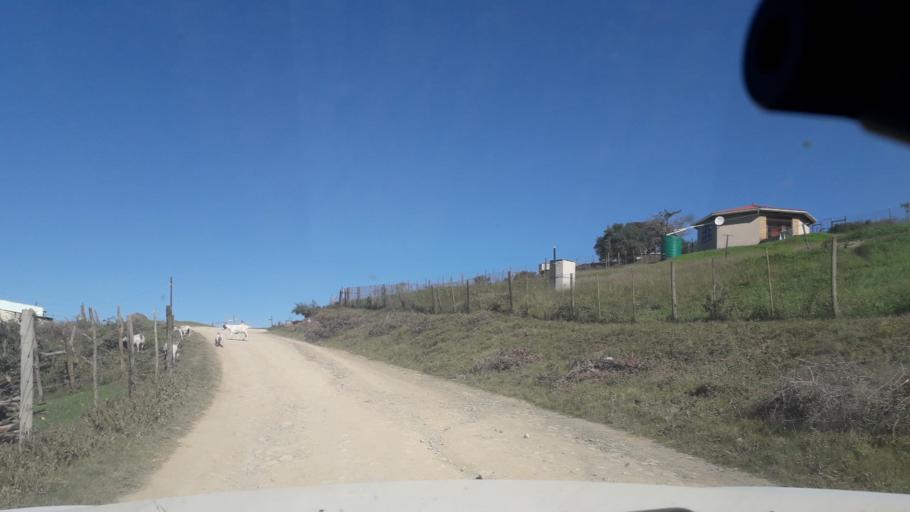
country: ZA
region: Eastern Cape
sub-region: Amathole District Municipality
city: Komga
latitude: -32.7663
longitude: 27.9481
